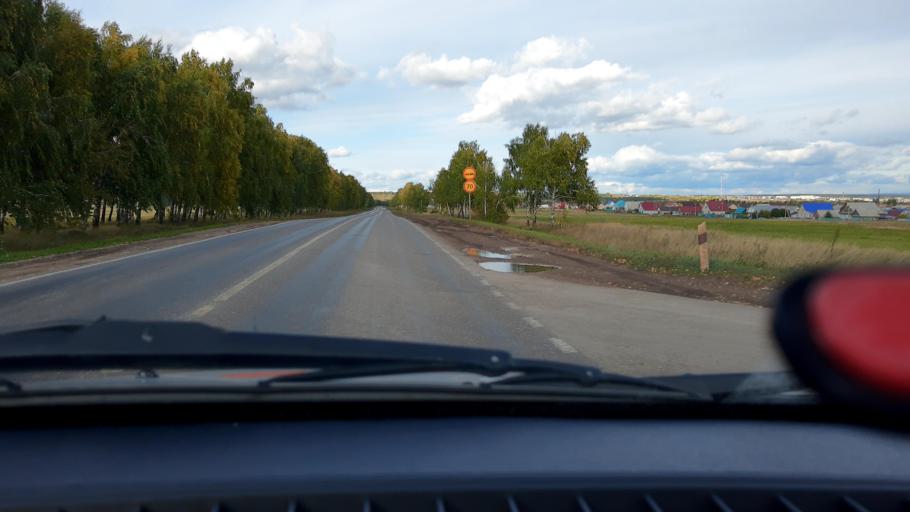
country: RU
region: Bashkortostan
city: Davlekanovo
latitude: 54.2011
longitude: 54.9803
